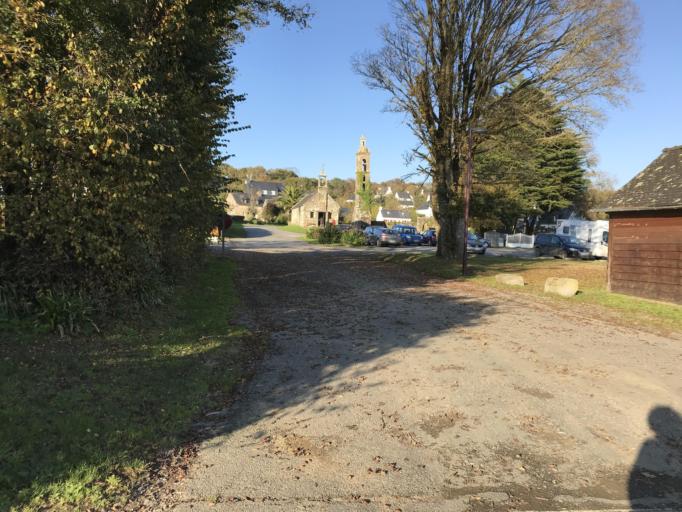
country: FR
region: Brittany
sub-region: Departement du Finistere
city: Hopital-Camfrout
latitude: 48.2968
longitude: -4.2253
